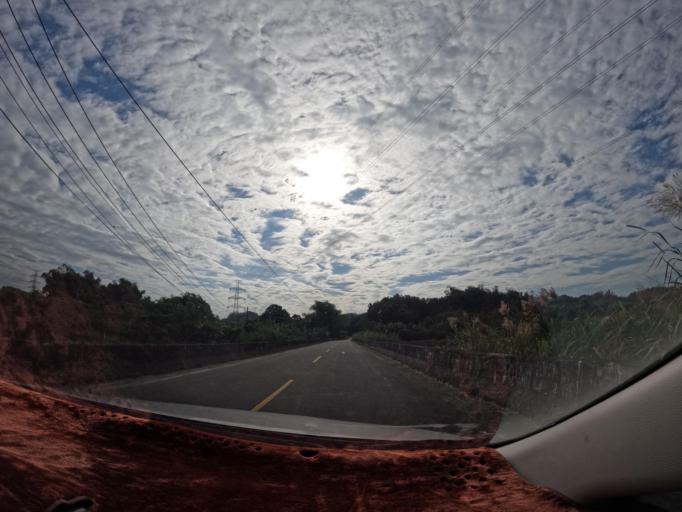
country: TW
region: Taiwan
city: Yujing
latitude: 23.0310
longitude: 120.4158
